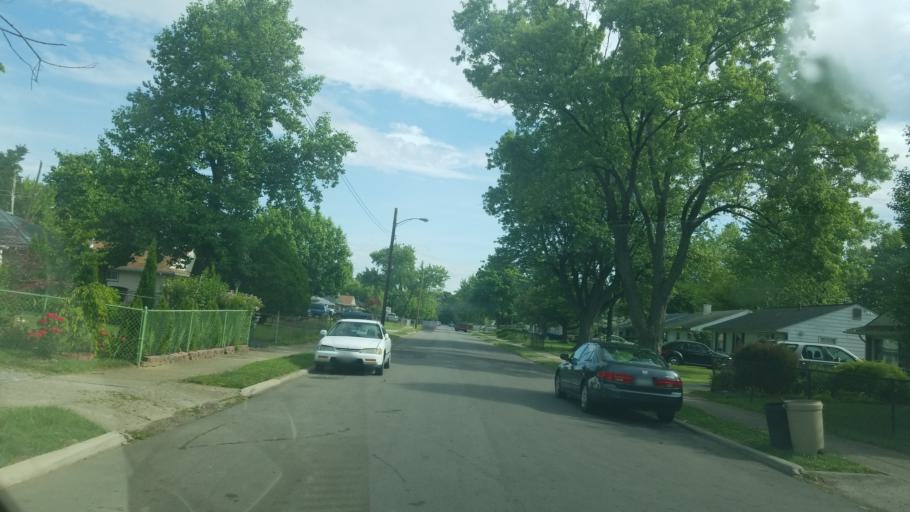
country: US
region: Ohio
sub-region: Franklin County
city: Minerva Park
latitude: 40.0367
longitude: -82.9737
